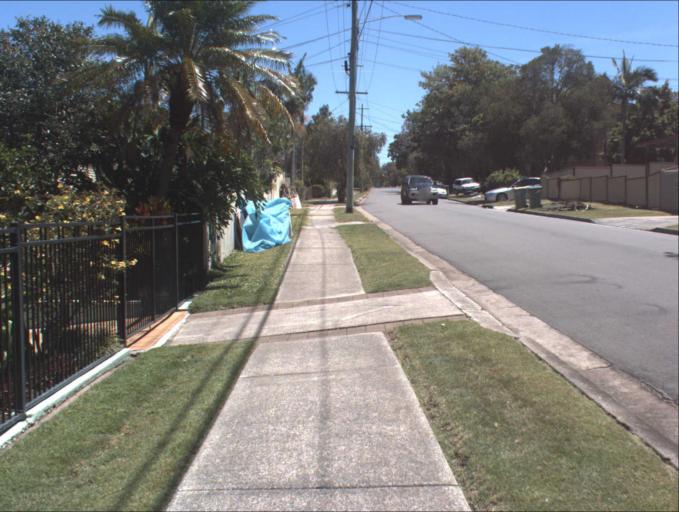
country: AU
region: Queensland
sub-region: Logan
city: Logan City
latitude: -27.6410
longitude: 153.1242
